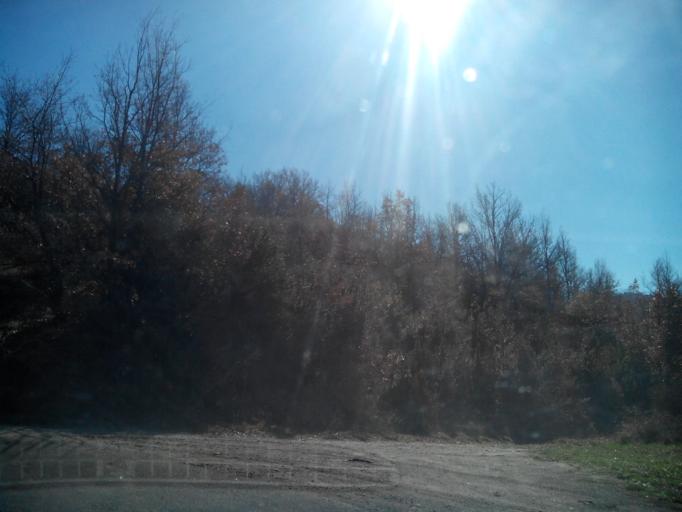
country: ES
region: Catalonia
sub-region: Provincia de Lleida
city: Lles de Cerdanya
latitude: 42.3668
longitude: 1.6857
